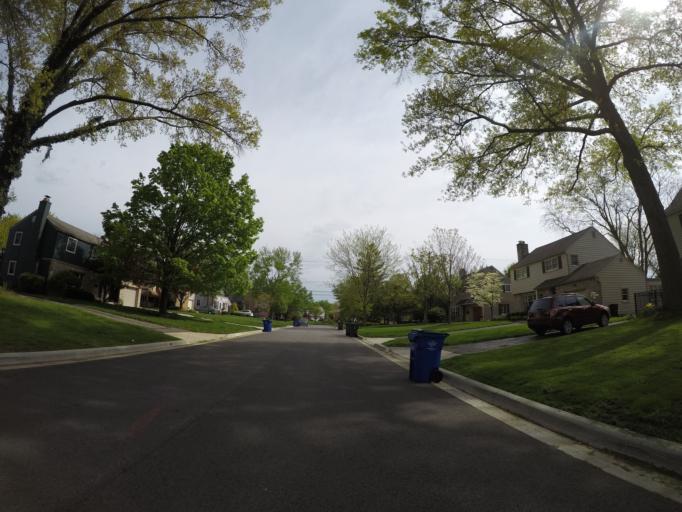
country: US
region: Ohio
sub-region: Franklin County
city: Upper Arlington
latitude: 39.9980
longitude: -83.0540
